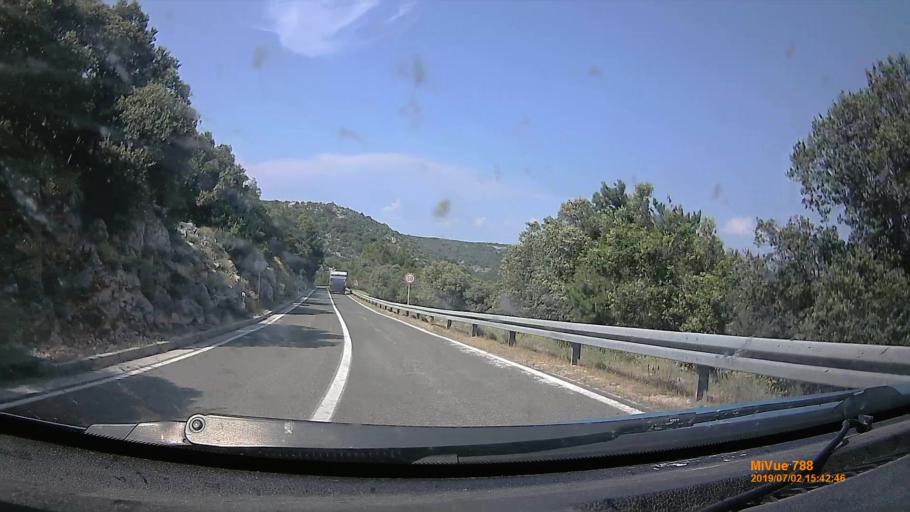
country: HR
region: Primorsko-Goranska
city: Cres
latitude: 44.9554
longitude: 14.4530
